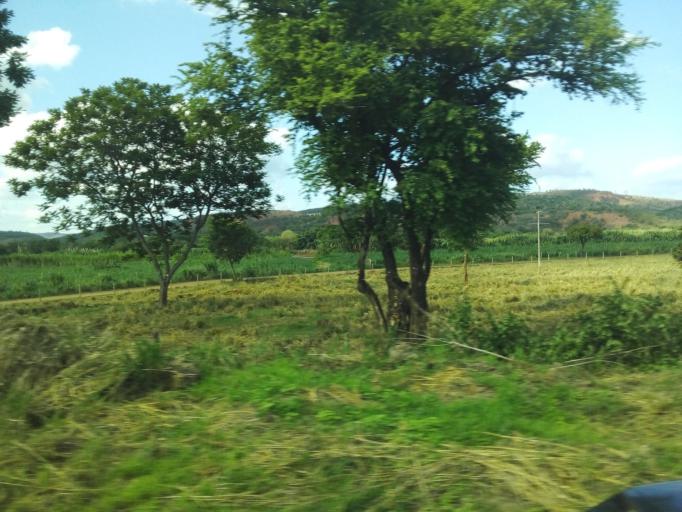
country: BR
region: Minas Gerais
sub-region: Conselheiro Pena
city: Conselheiro Pena
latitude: -18.9841
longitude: -41.6058
